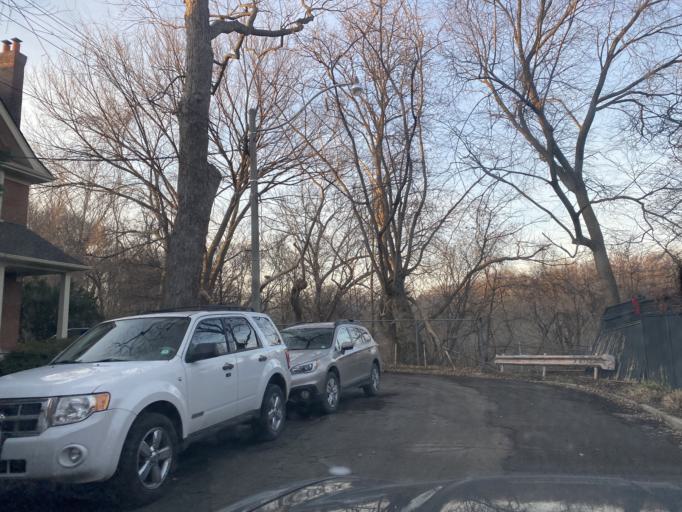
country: CA
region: Ontario
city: Toronto
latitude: 43.6700
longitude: -79.3638
